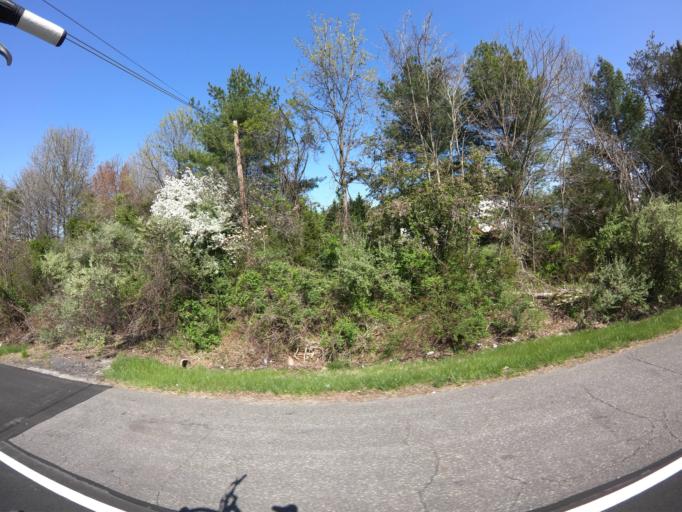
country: US
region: Delaware
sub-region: New Castle County
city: Newark
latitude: 39.6445
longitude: -75.7795
